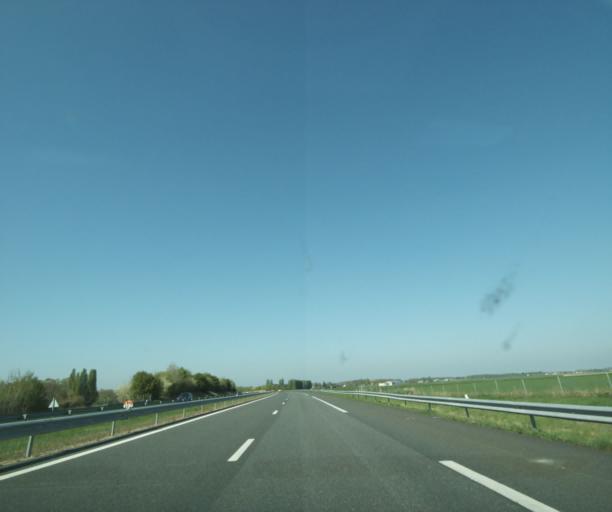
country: FR
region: Centre
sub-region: Departement du Loiret
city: Vimory
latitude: 47.9552
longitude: 2.6742
